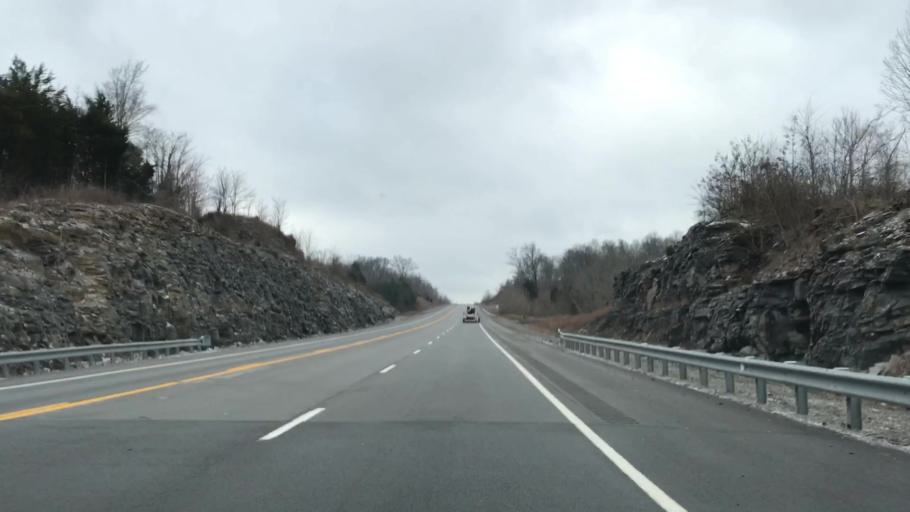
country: US
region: Kentucky
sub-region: Adair County
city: Columbia
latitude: 37.0315
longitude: -85.3816
